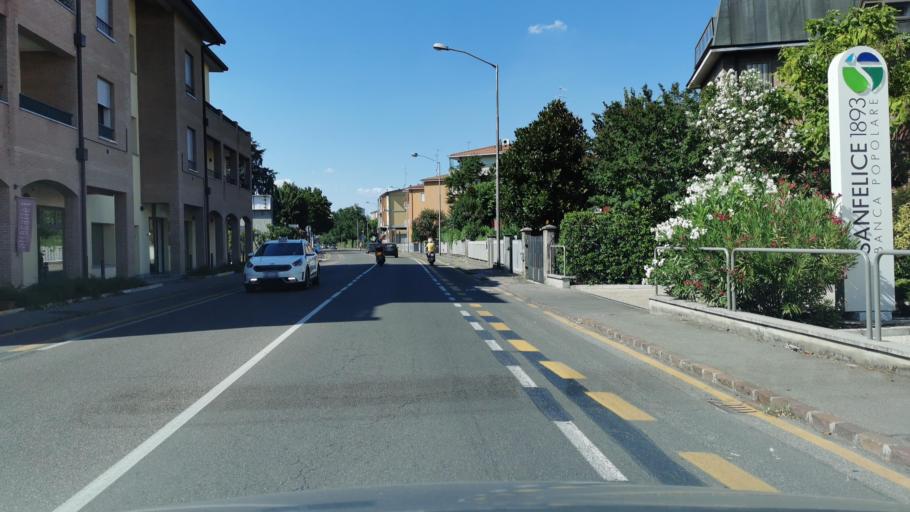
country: IT
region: Emilia-Romagna
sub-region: Provincia di Modena
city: Modena
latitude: 44.6252
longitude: 10.9272
